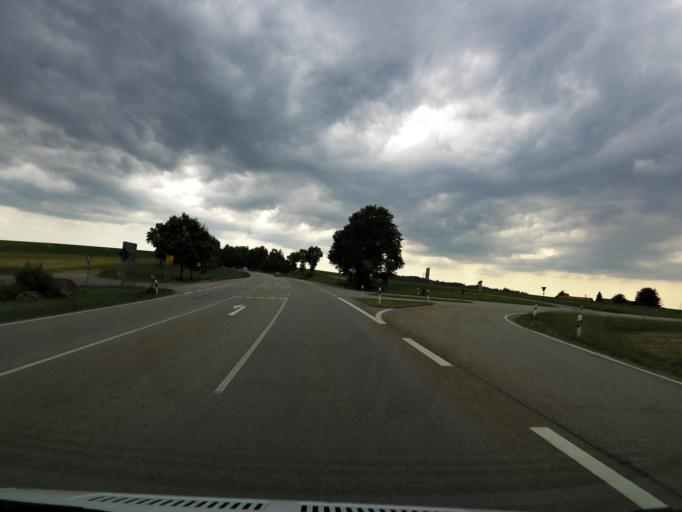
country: DE
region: Bavaria
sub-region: Lower Bavaria
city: Buchlberg
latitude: 48.7002
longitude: 13.5107
